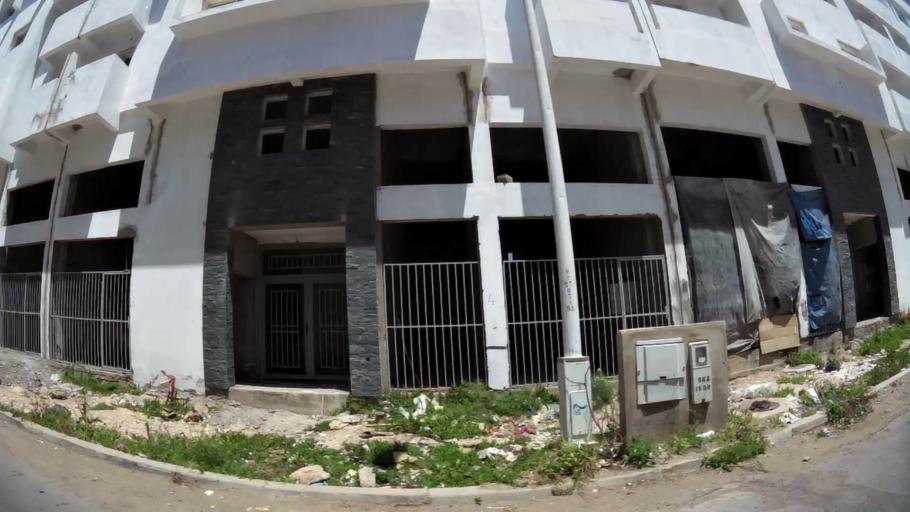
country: MA
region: Oued ed Dahab-Lagouira
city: Dakhla
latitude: 30.4387
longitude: -9.5596
